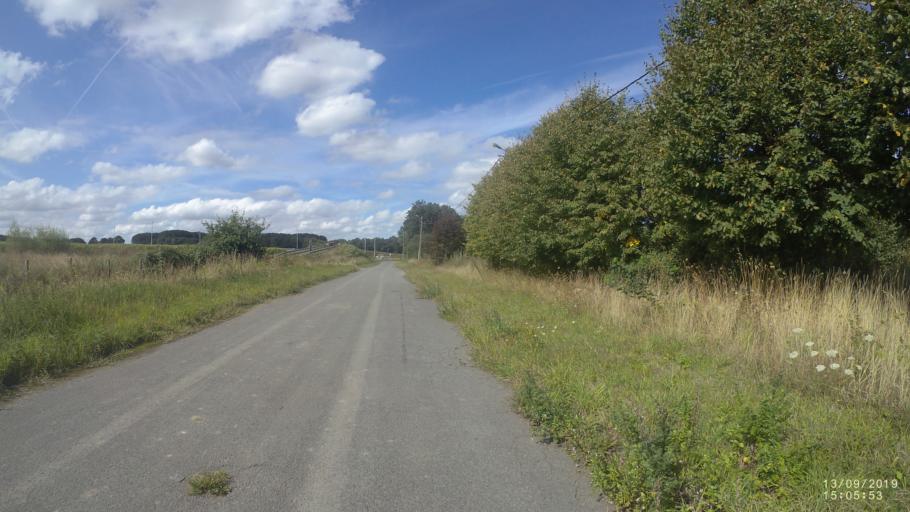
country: BE
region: Flanders
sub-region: Provincie Oost-Vlaanderen
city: Zelzate
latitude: 51.1906
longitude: 3.7776
